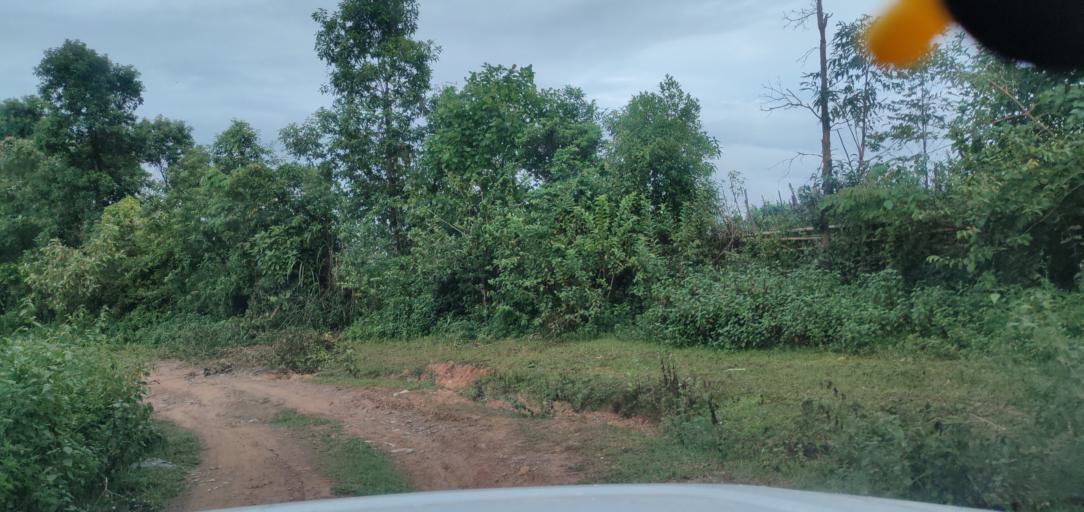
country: LA
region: Phongsali
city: Phongsali
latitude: 21.4328
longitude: 102.2611
